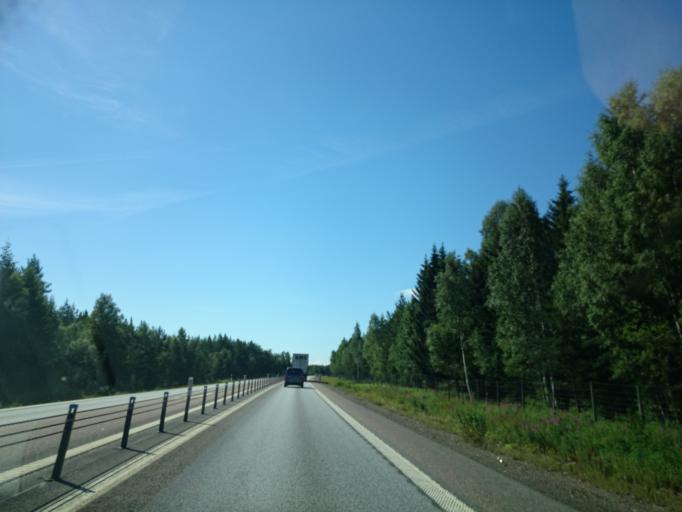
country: SE
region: Gaevleborg
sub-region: Gavle Kommun
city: Norrsundet
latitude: 60.8242
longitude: 17.0842
